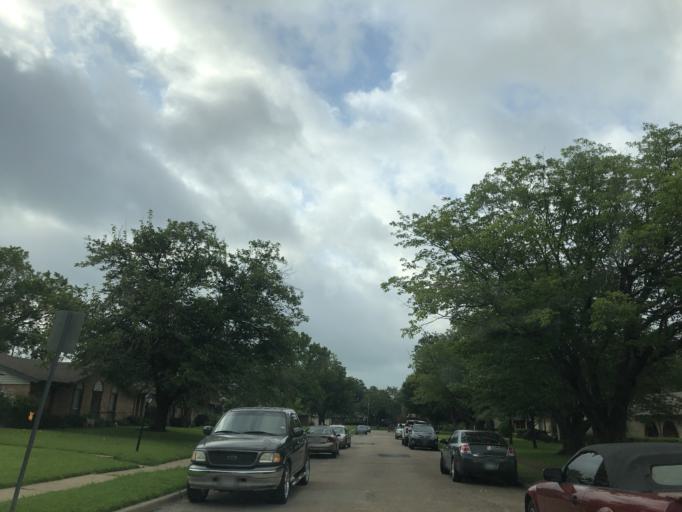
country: US
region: Texas
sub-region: Dallas County
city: Mesquite
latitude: 32.8323
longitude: -96.6395
